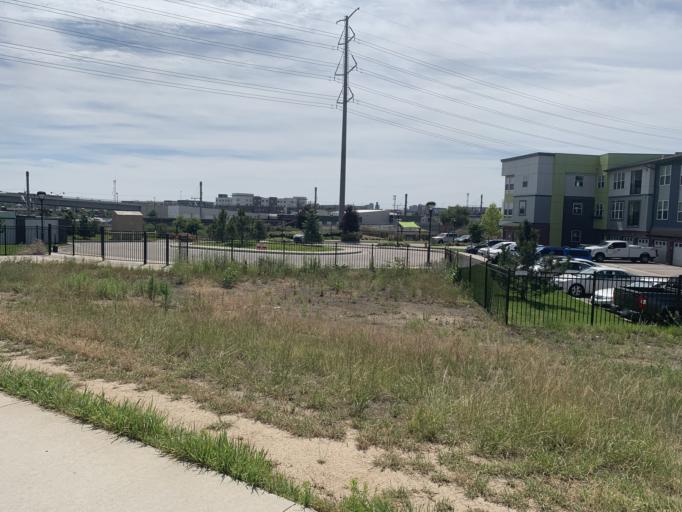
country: US
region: Colorado
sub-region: Denver County
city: Denver
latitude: 39.7660
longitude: -104.9990
